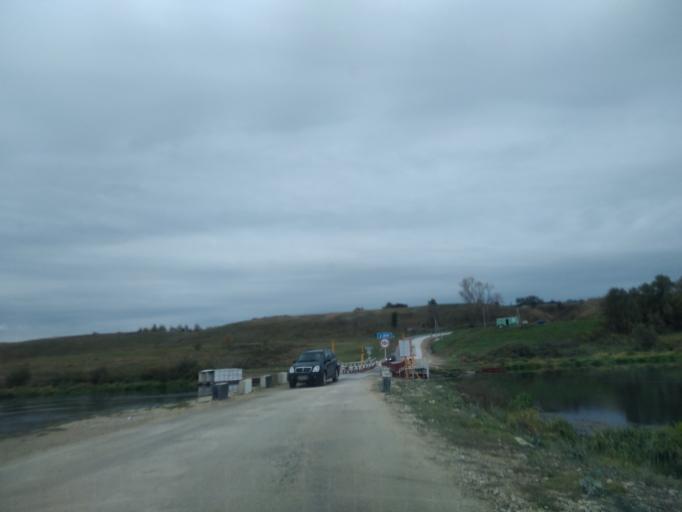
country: RU
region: Lipetsk
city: Zadonsk
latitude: 52.3212
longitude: 38.9229
